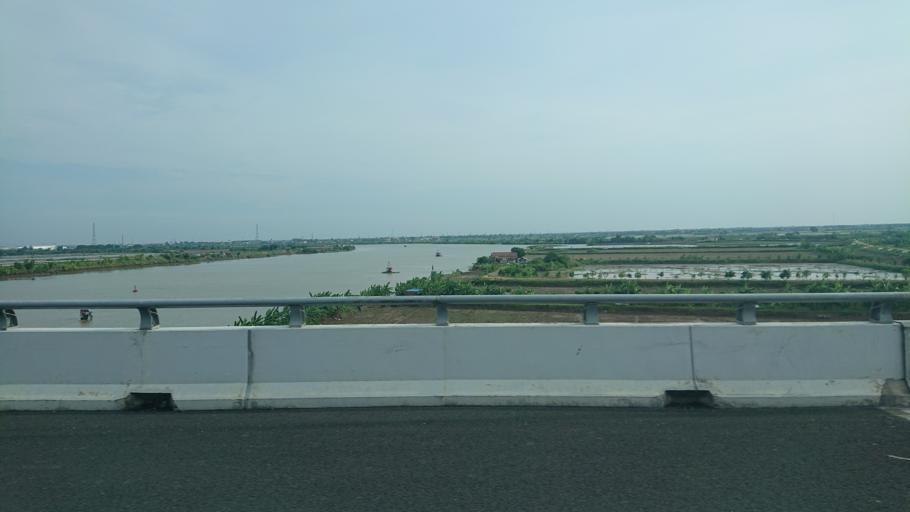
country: VN
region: Hai Phong
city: An Lao
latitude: 20.8084
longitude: 106.5113
